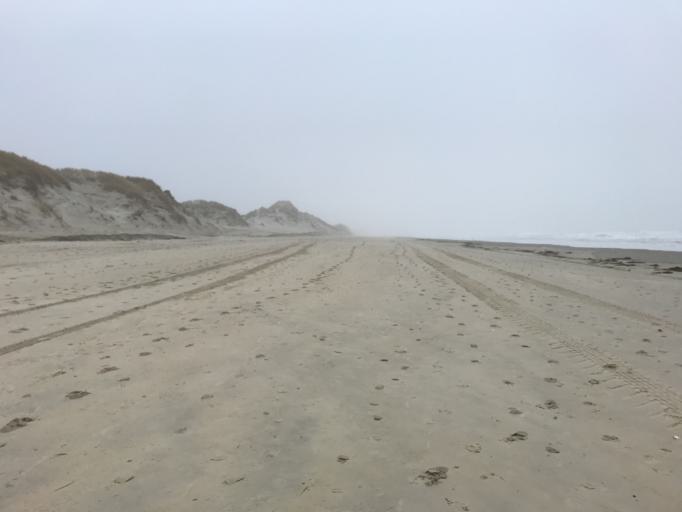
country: DE
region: Lower Saxony
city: Borkum
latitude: 53.6157
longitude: 6.7461
